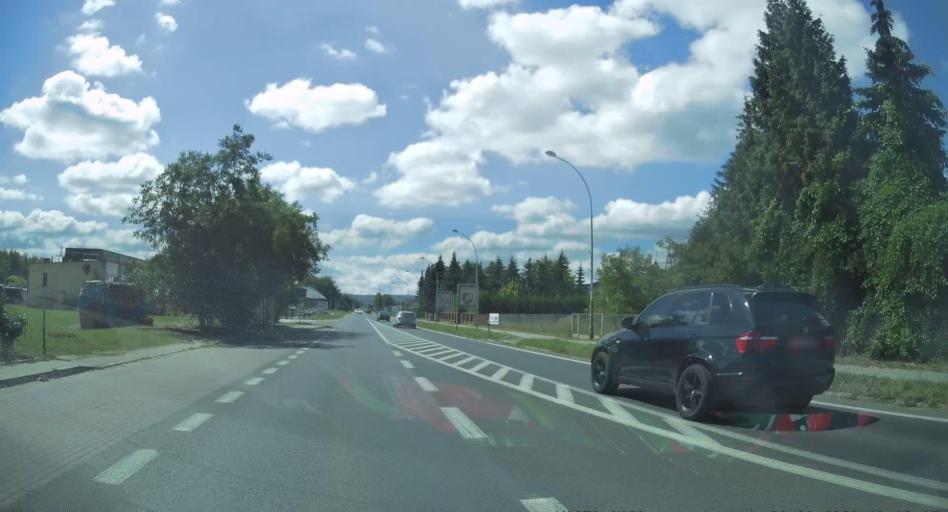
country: PL
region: Subcarpathian Voivodeship
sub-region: Powiat debicki
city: Brzeznica
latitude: 50.0727
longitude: 21.4498
